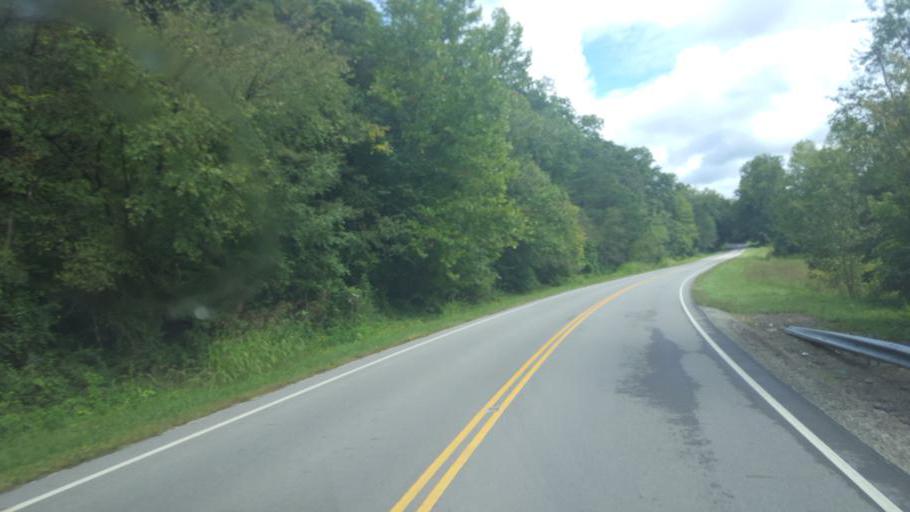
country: US
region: Ohio
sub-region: Scioto County
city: Sciotodale
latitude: 38.8869
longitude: -82.7845
